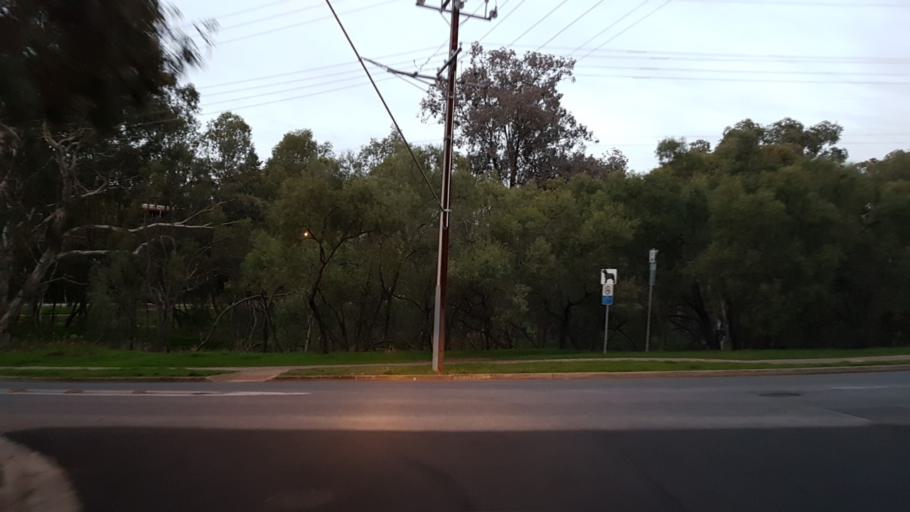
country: AU
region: South Australia
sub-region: Port Adelaide Enfield
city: Gilles Plains
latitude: -34.8392
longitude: 138.6536
